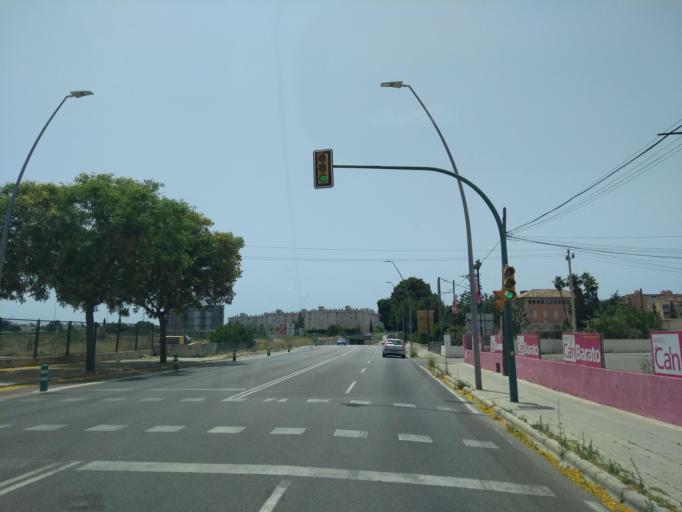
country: ES
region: Balearic Islands
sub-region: Illes Balears
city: Palma
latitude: 39.5904
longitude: 2.6669
